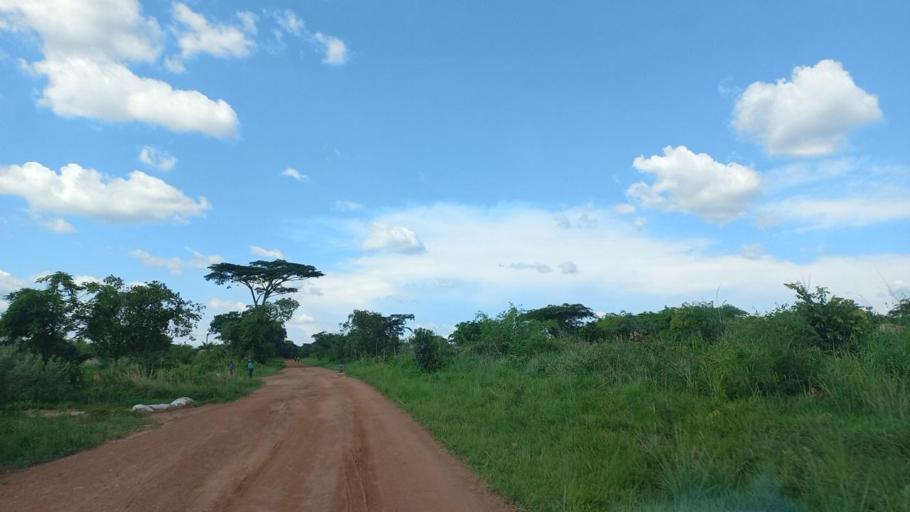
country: ZM
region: Copperbelt
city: Kitwe
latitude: -12.8466
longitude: 28.3930
